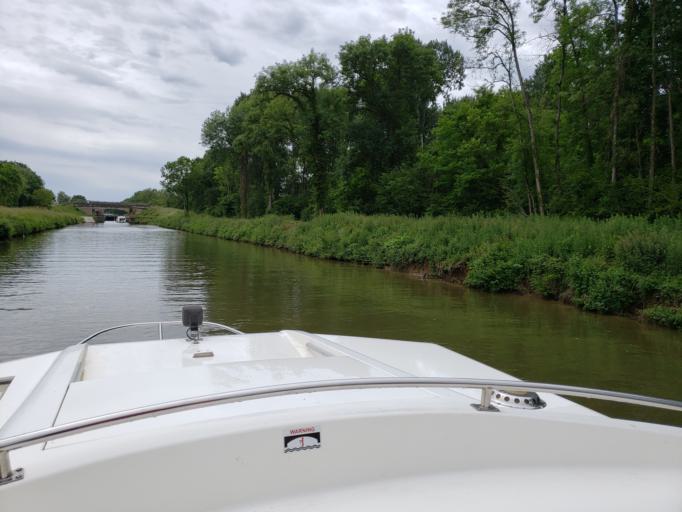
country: FR
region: Bourgogne
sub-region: Departement de l'Yonne
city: Appoigny
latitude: 47.8986
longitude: 3.5360
